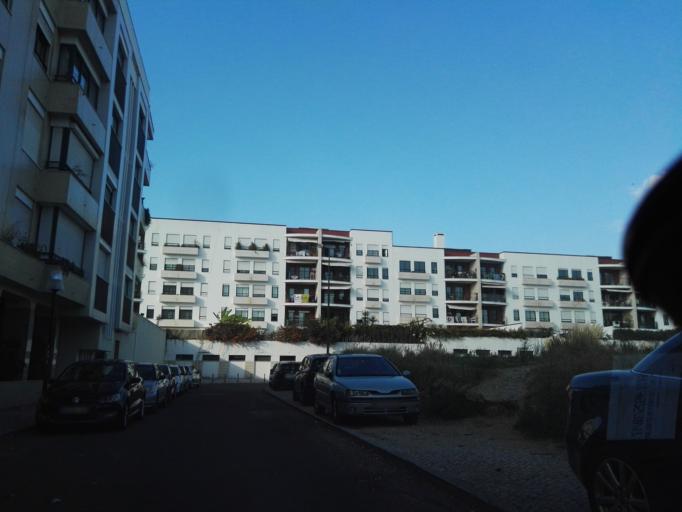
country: PT
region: Lisbon
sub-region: Odivelas
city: Olival do Basto
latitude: 38.7659
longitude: -9.1518
